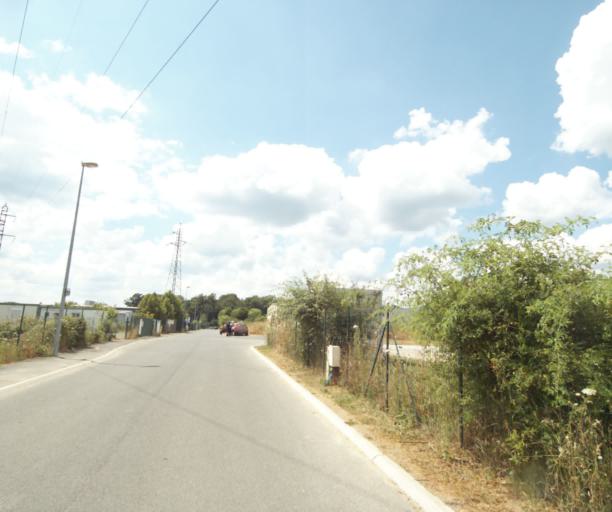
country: FR
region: Ile-de-France
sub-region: Departement de Seine-et-Marne
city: Vulaines-sur-Seine
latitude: 48.4256
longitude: 2.7725
